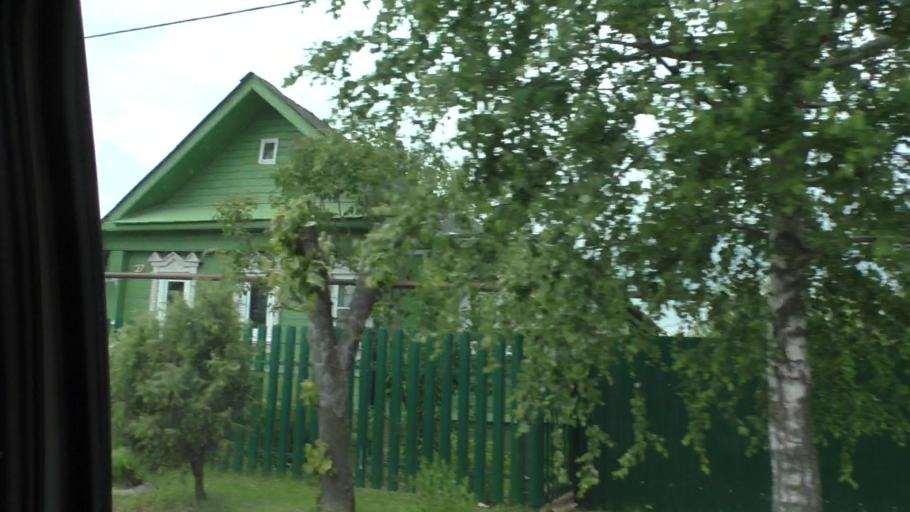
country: RU
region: Moskovskaya
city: Il'inskiy Pogost
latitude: 55.4723
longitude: 38.8943
